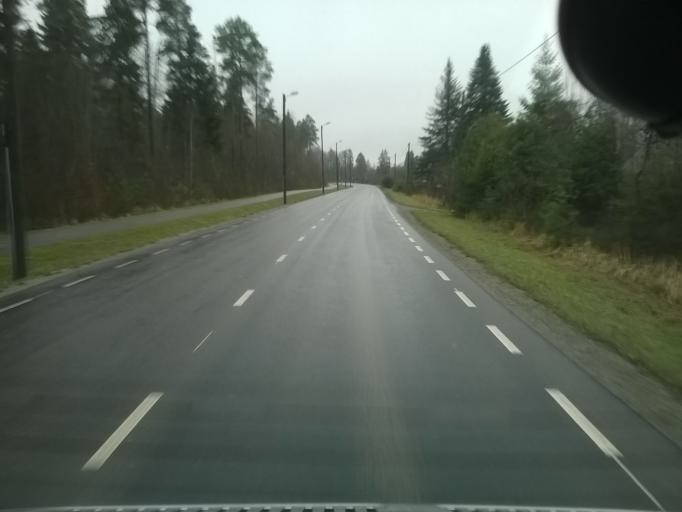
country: EE
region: Harju
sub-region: Saku vald
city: Saku
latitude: 59.2247
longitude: 24.6733
